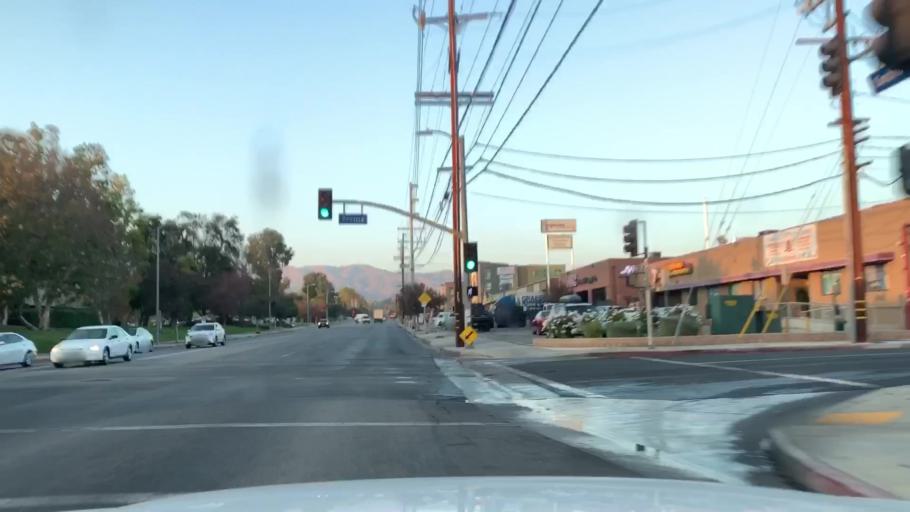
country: US
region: California
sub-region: Los Angeles County
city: Northridge
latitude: 34.2390
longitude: -118.5623
